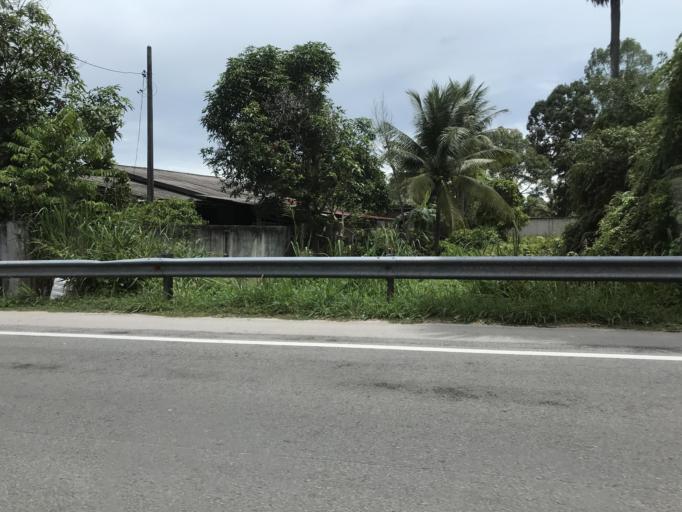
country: MY
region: Kelantan
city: Tumpat
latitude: 6.1777
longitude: 102.1802
